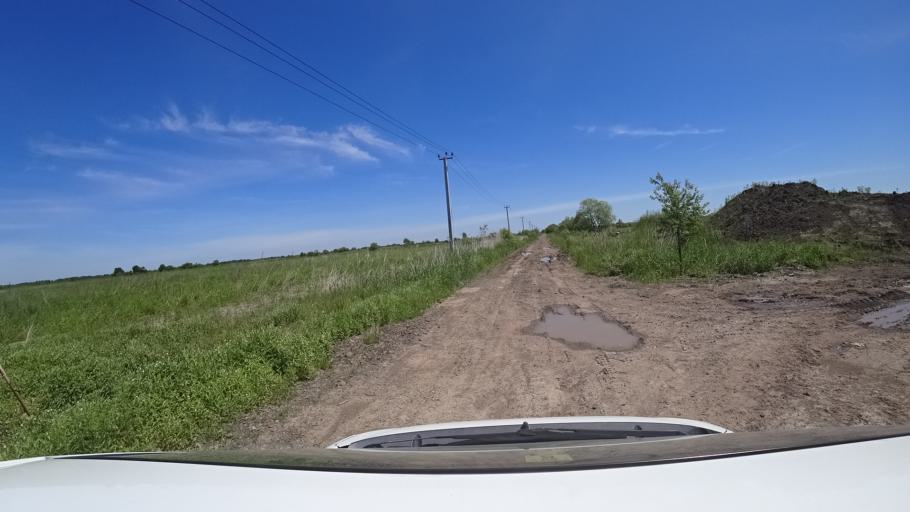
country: RU
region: Khabarovsk Krai
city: Topolevo
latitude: 48.4992
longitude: 135.2043
